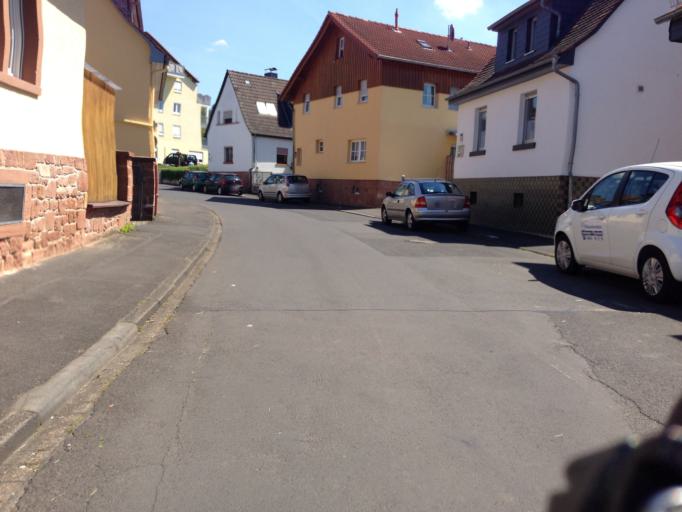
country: DE
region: Hesse
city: Budingen
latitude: 50.2862
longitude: 9.1115
